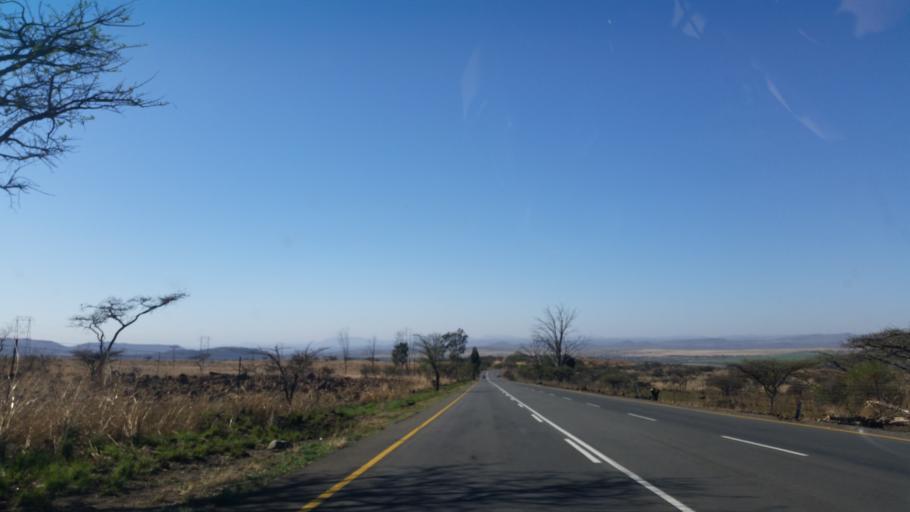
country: ZA
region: KwaZulu-Natal
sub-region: uThukela District Municipality
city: Ladysmith
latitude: -28.6990
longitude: 29.7726
